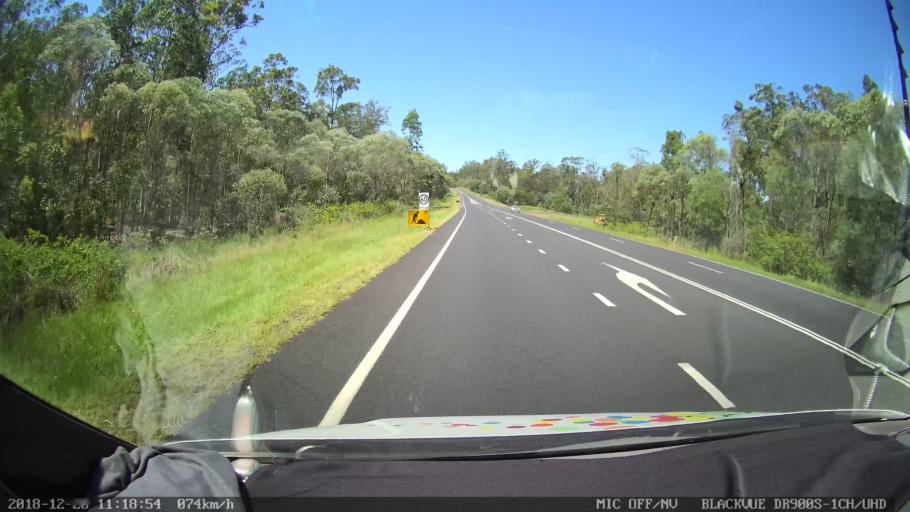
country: AU
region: New South Wales
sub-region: Richmond Valley
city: Casino
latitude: -29.0567
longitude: 153.0056
